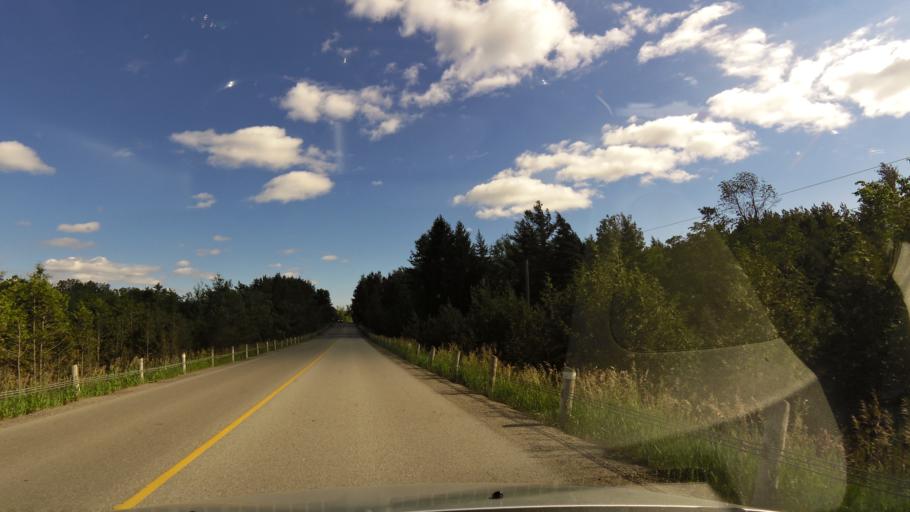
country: CA
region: Ontario
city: Bradford West Gwillimbury
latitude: 44.1908
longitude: -79.6227
